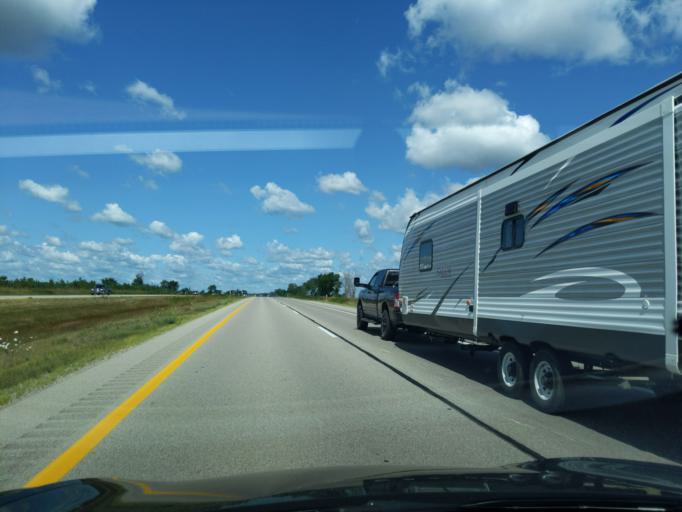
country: US
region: Michigan
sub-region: Isabella County
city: Shepherd
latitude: 43.5449
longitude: -84.6897
